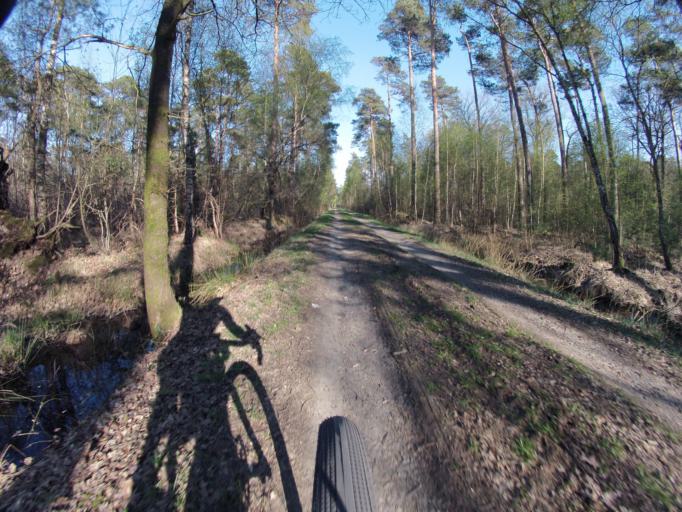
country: DE
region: Lower Saxony
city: Schuttorf
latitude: 52.3611
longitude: 7.2428
